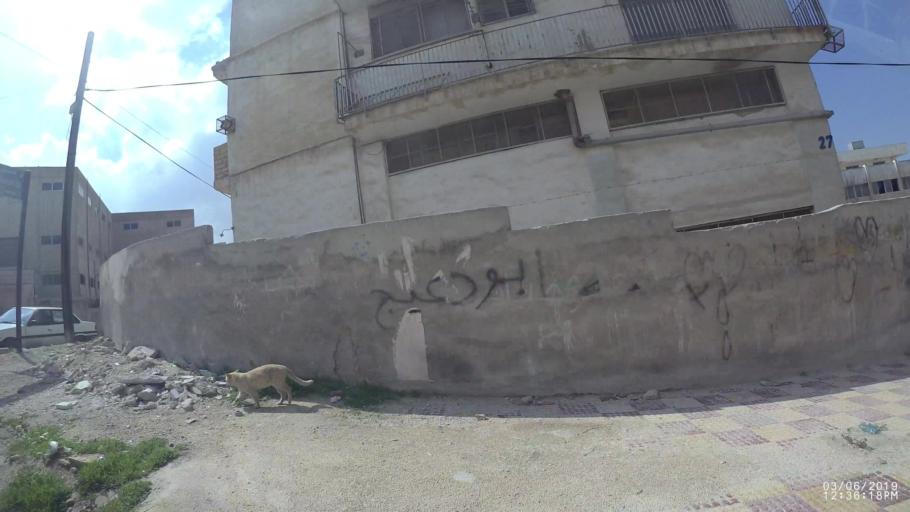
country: JO
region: Zarqa
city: Russeifa
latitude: 31.9920
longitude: 35.9958
